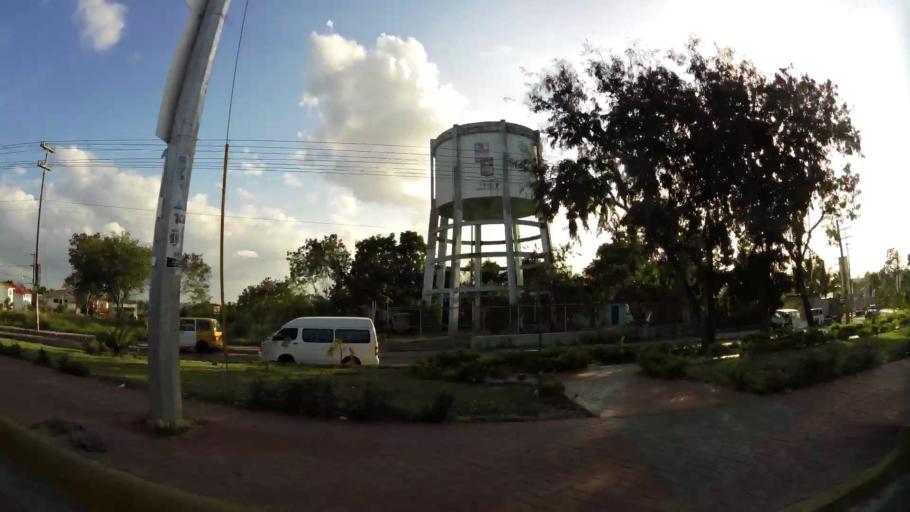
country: DO
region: Nacional
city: La Agustina
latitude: 18.5469
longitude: -69.9223
